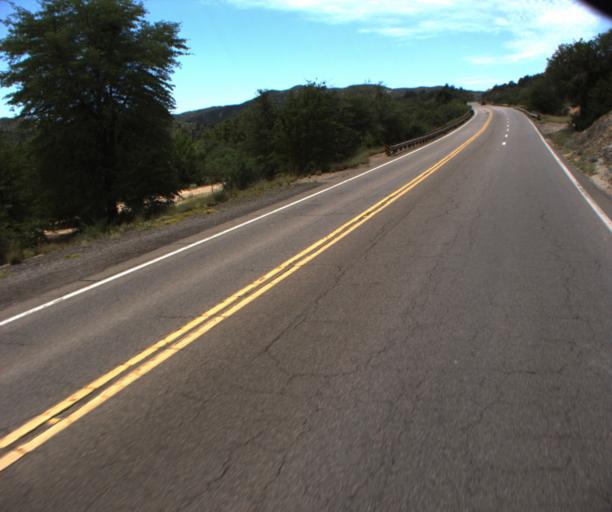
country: US
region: Arizona
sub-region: Gila County
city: Miami
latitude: 33.3752
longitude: -110.9149
